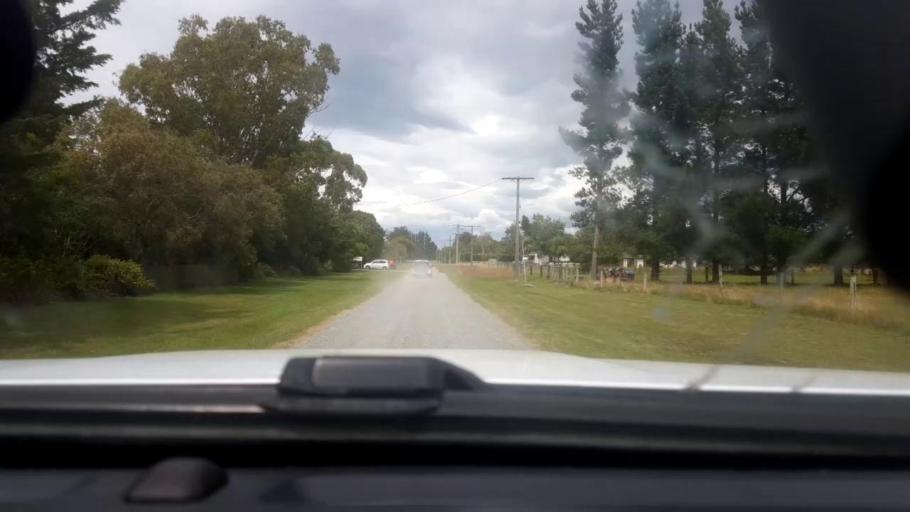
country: NZ
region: Canterbury
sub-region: Timaru District
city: Pleasant Point
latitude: -44.1403
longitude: 171.2907
